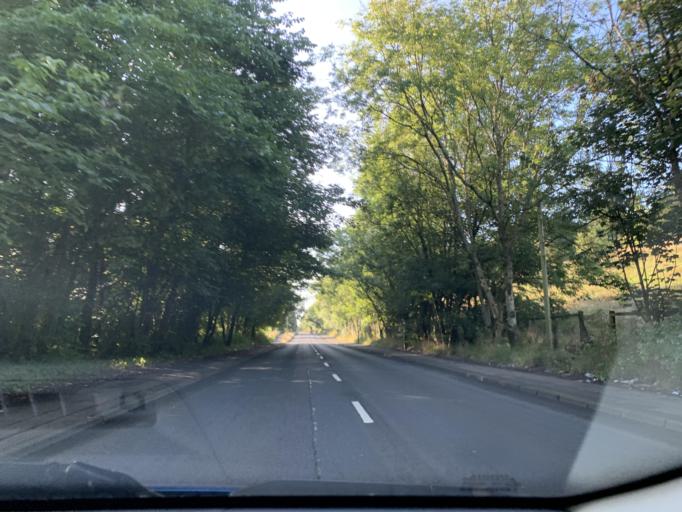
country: GB
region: Scotland
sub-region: East Renfrewshire
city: Giffnock
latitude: 55.8173
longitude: -4.3308
